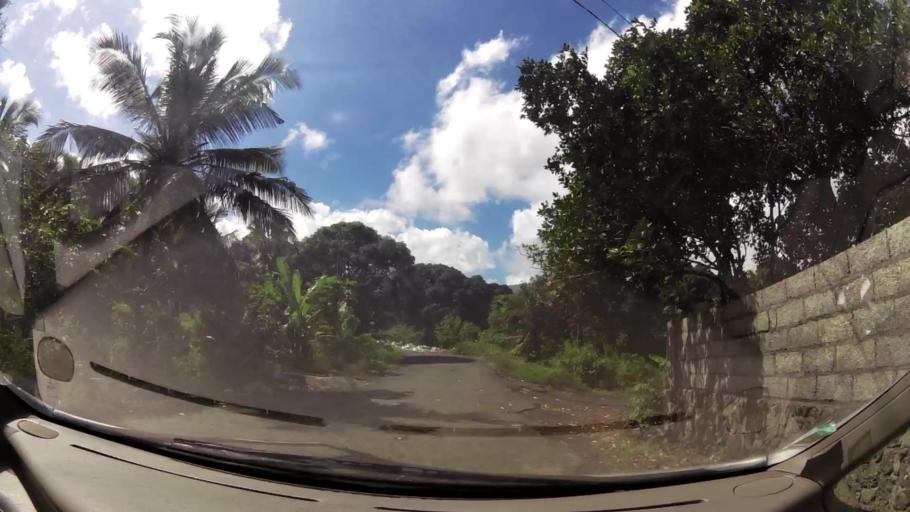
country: KM
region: Grande Comore
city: Mavingouni
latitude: -11.7407
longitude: 43.2455
